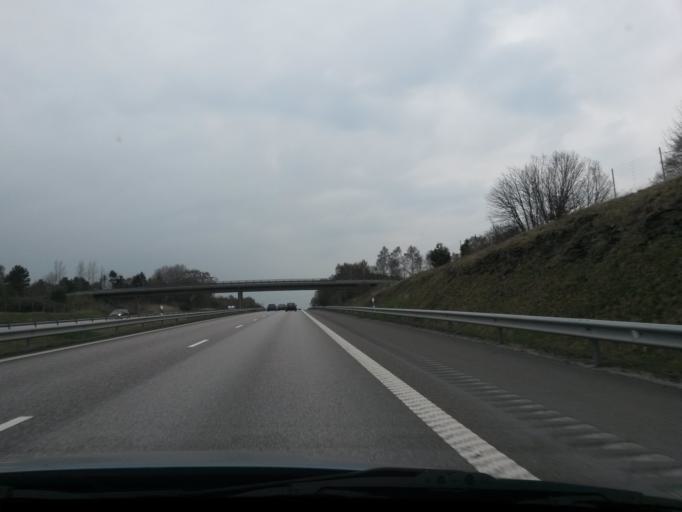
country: SE
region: Halland
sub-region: Kungsbacka Kommun
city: Frillesas
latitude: 57.2698
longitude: 12.2156
